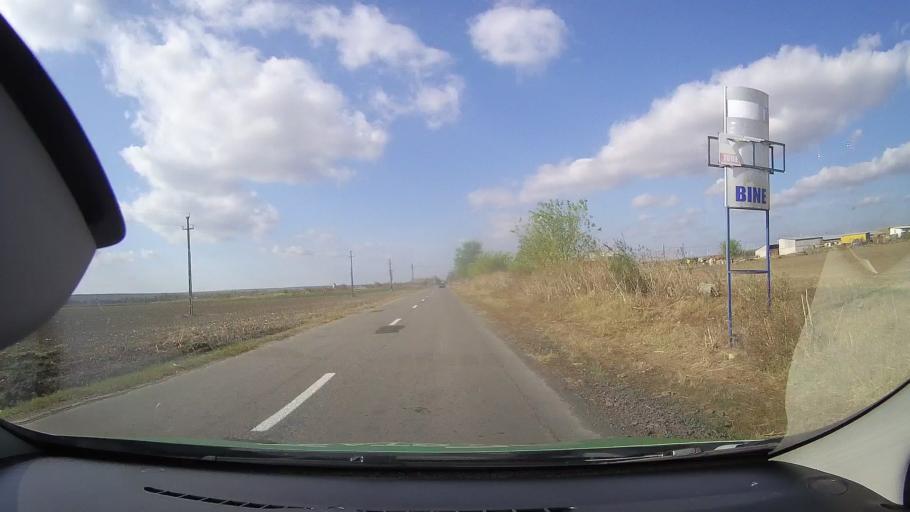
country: RO
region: Constanta
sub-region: Comuna Istria
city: Nuntasi
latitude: 44.5346
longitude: 28.6633
